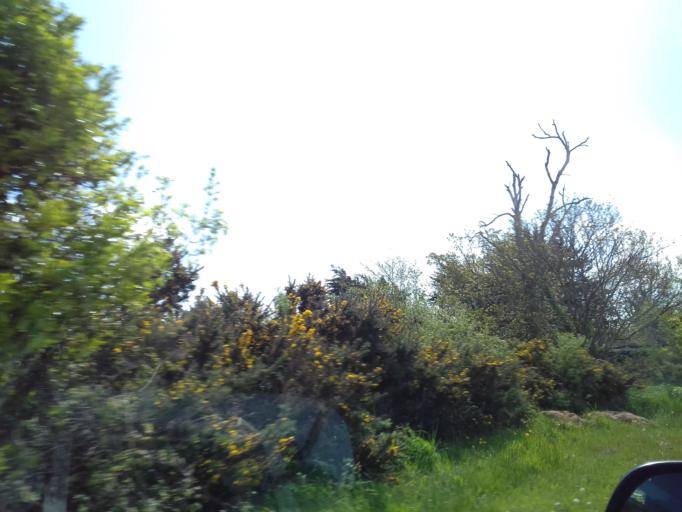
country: IE
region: Leinster
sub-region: Loch Garman
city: Castlebridge
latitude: 52.3747
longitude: -6.4488
